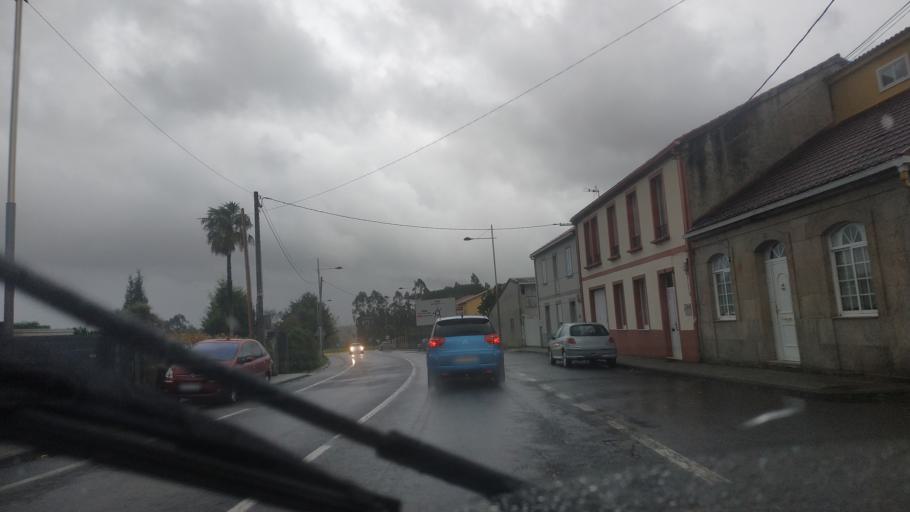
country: ES
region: Galicia
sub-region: Provincia da Coruna
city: Negreira
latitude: 42.9221
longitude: -8.7344
